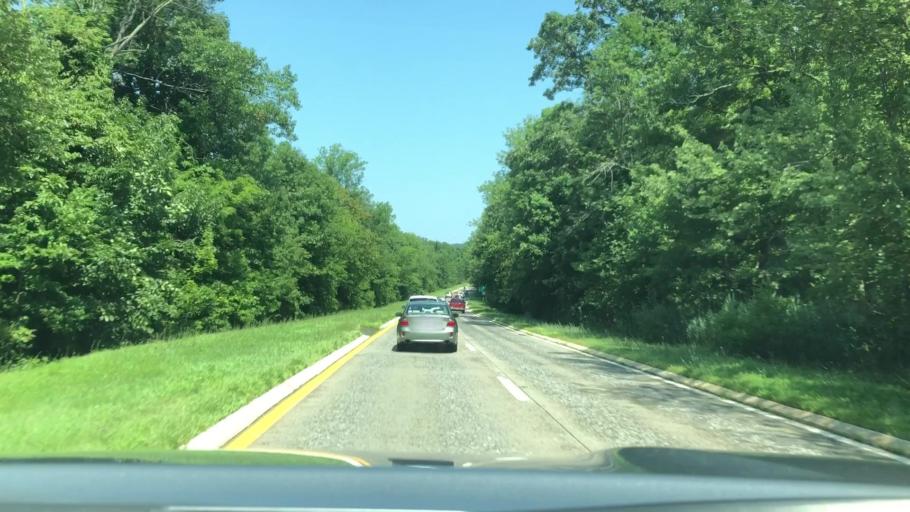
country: US
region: New York
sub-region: Rockland County
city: Mount Ivy
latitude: 41.1772
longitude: -74.0359
